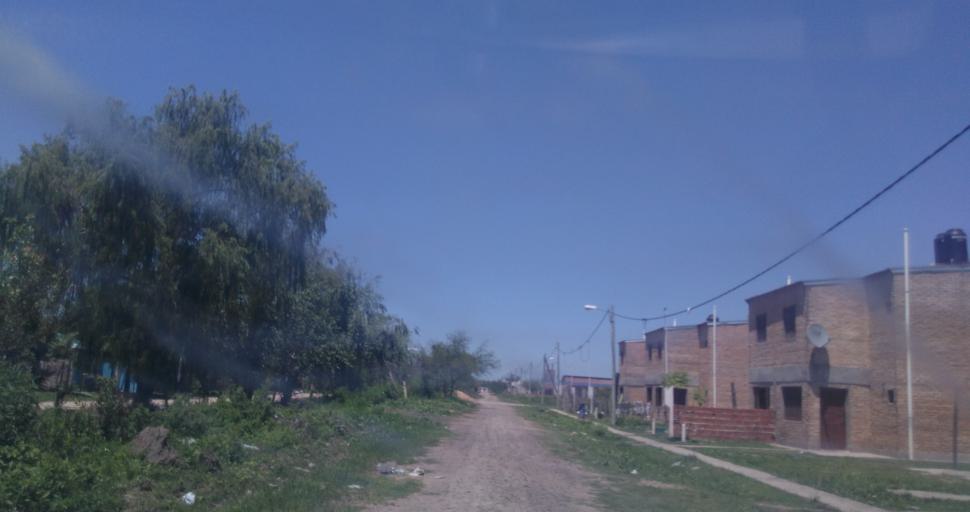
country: AR
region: Chaco
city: Resistencia
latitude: -27.4786
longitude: -59.0131
